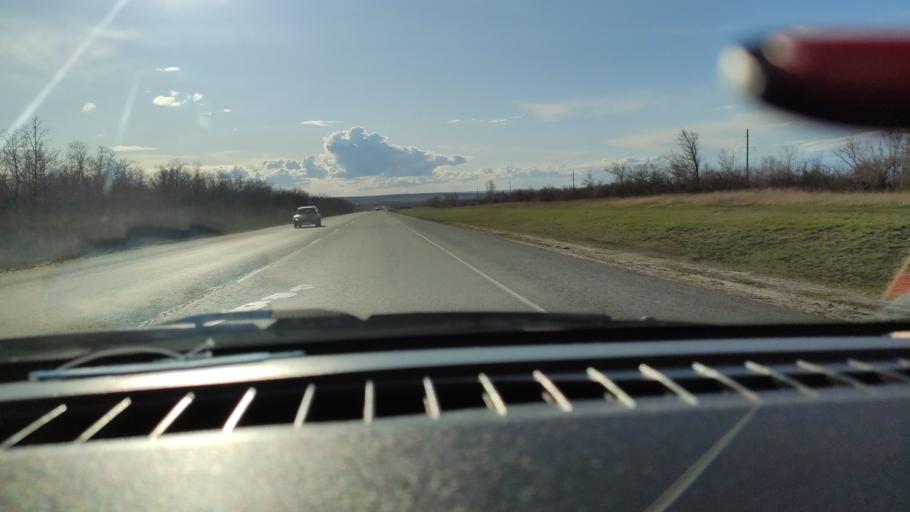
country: RU
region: Saratov
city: Yelshanka
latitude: 51.8272
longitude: 46.2720
